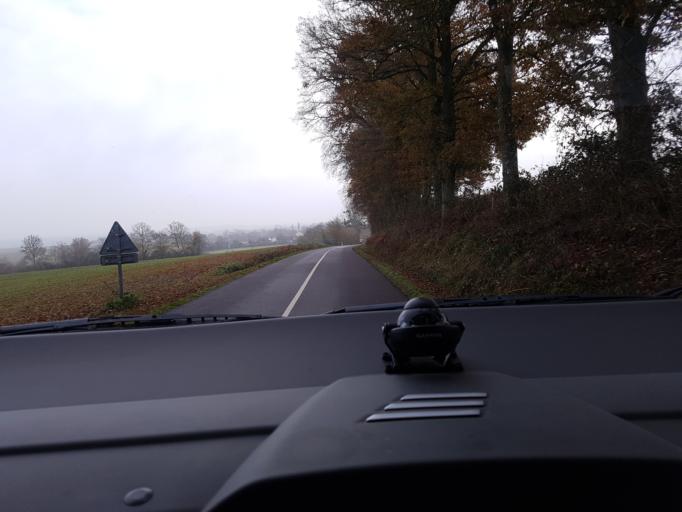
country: FR
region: Lower Normandy
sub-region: Departement de l'Orne
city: Mortree
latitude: 48.6344
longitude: 0.0253
